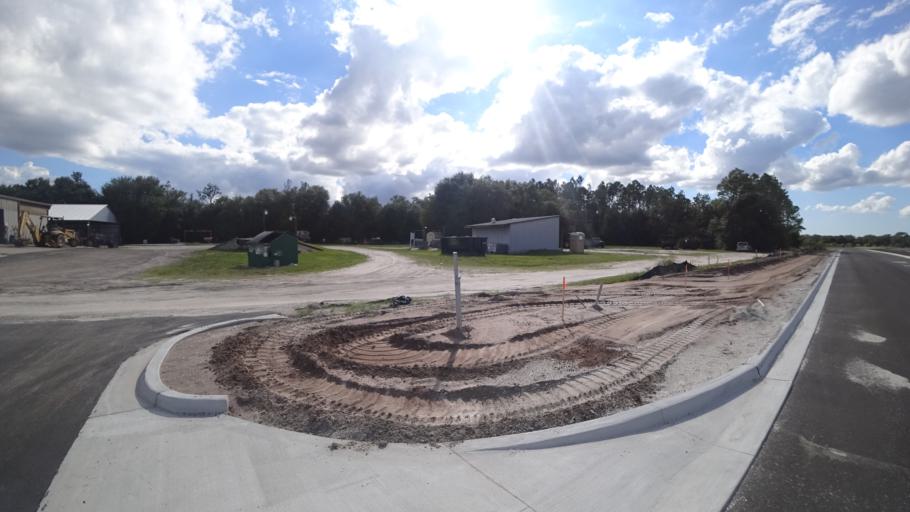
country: US
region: Florida
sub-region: Sarasota County
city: The Meadows
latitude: 27.4552
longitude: -82.3969
